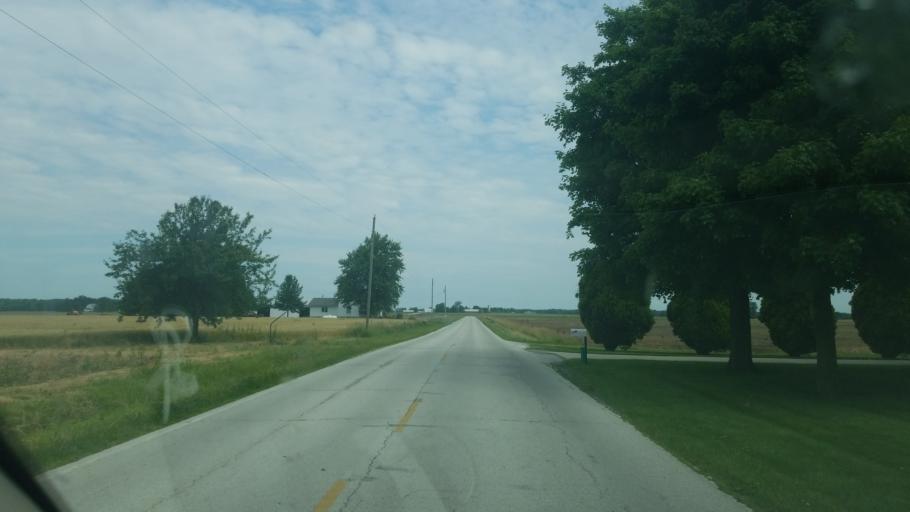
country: US
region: Ohio
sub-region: Seneca County
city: Fostoria
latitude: 41.0732
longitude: -83.4774
